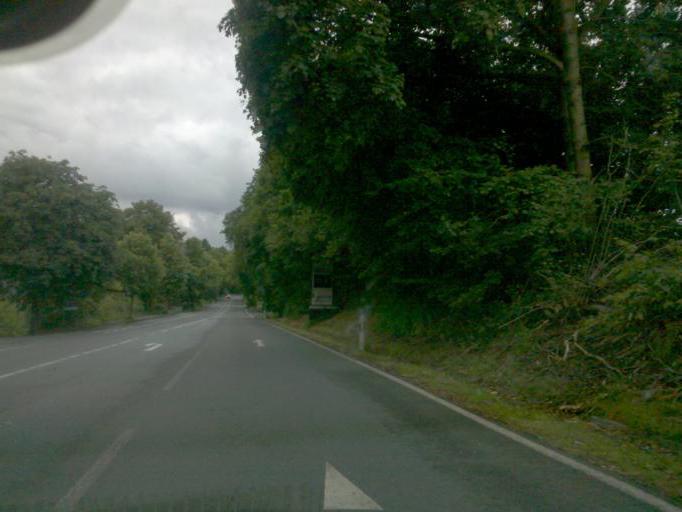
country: DE
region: North Rhine-Westphalia
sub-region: Regierungsbezirk Arnsberg
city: Meschede
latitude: 51.3391
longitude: 8.2689
